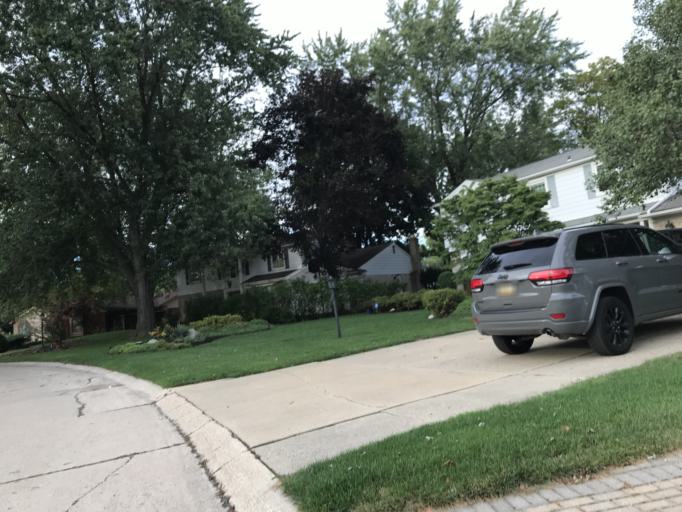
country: US
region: Michigan
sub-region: Oakland County
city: Franklin
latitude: 42.4834
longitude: -83.3264
